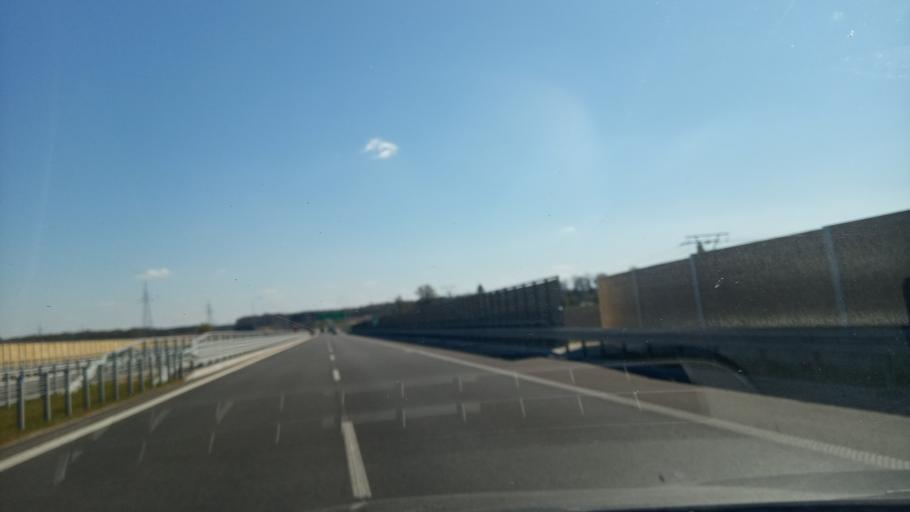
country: PL
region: West Pomeranian Voivodeship
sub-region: Powiat szczecinecki
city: Szczecinek
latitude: 53.6970
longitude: 16.7300
